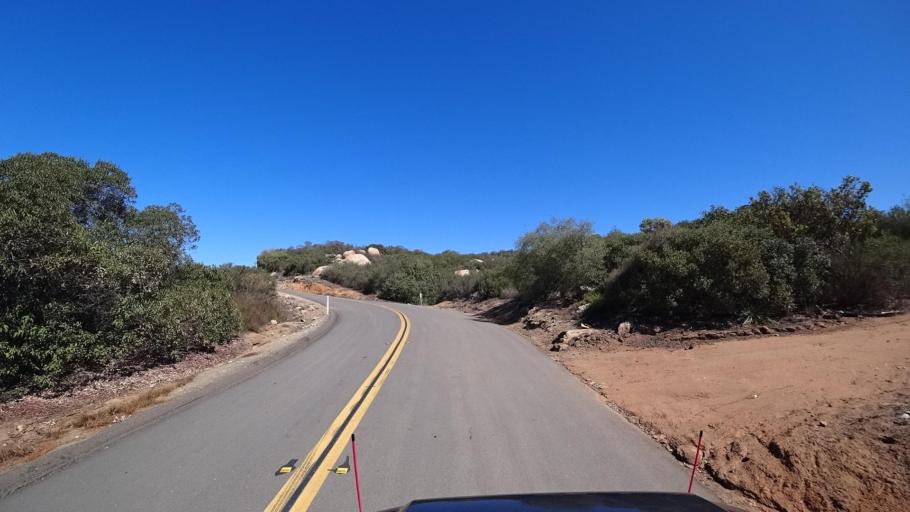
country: US
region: California
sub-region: San Diego County
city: Alpine
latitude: 32.7774
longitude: -116.7251
